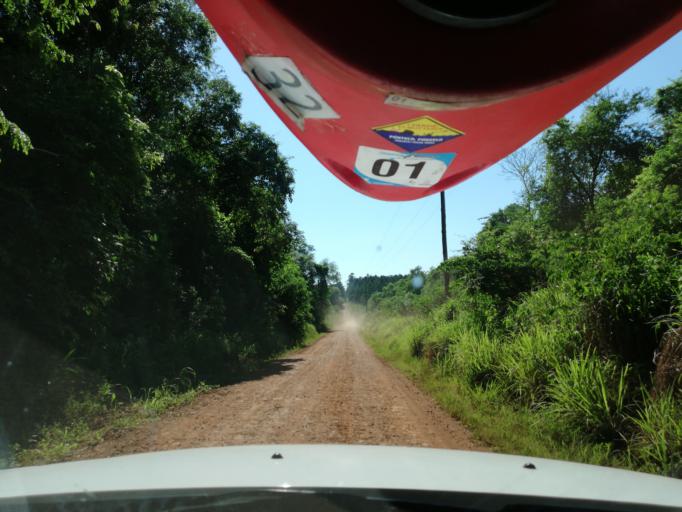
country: AR
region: Misiones
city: Puerto Leoni
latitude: -26.9694
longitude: -55.1639
